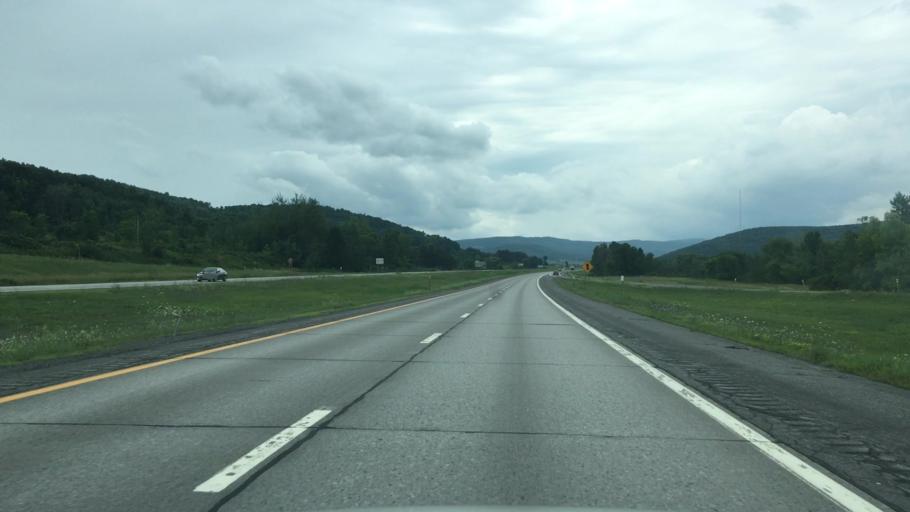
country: US
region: New York
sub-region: Schoharie County
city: Cobleskill
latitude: 42.6540
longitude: -74.5110
